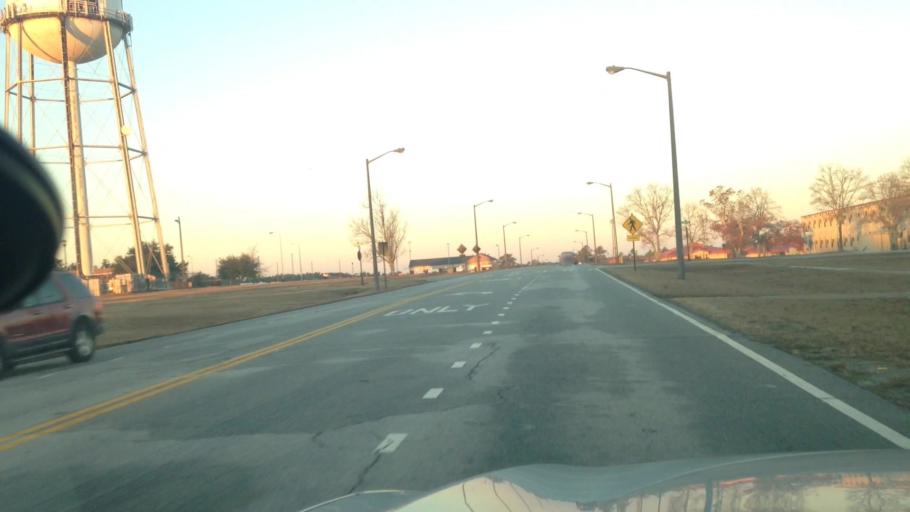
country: US
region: Georgia
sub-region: Columbia County
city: Grovetown
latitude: 33.4159
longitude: -82.1391
